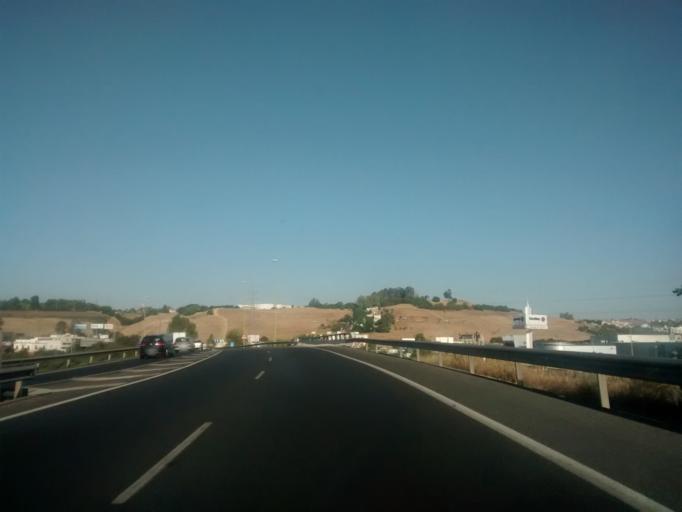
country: ES
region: Andalusia
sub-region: Provincia de Sevilla
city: Camas
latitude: 37.3904
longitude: -6.0262
